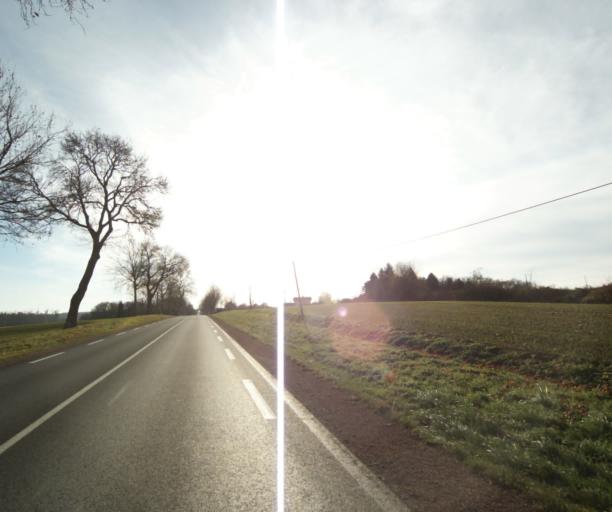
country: FR
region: Poitou-Charentes
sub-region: Departement de la Charente-Maritime
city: Saint-Hilaire-de-Villefranche
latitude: 45.8411
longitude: -0.5352
